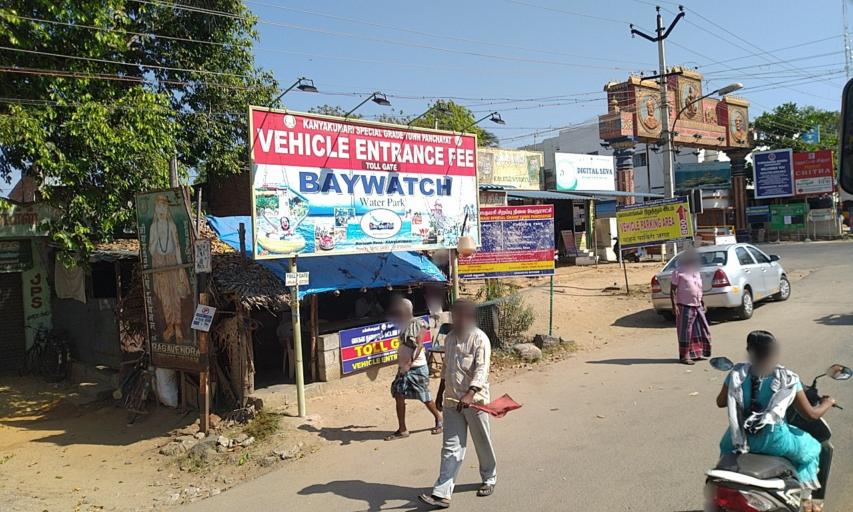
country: IN
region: Tamil Nadu
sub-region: Kanniyakumari
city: Kanniyakumari
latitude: 8.0926
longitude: 77.5493
